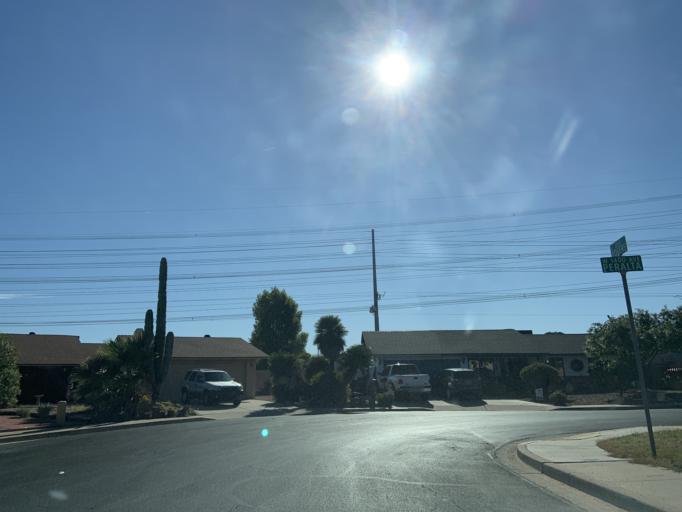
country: US
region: Arizona
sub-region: Maricopa County
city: San Carlos
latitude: 33.3577
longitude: -111.8639
